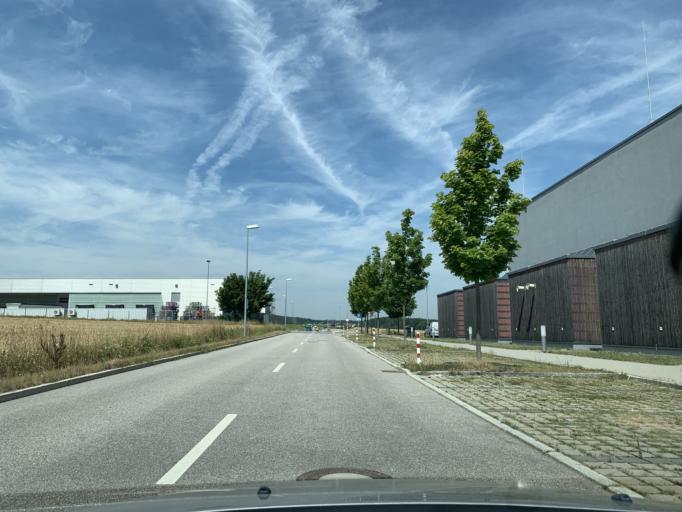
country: DE
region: Bavaria
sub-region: Lower Bavaria
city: Vilsbiburg
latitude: 48.4540
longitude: 12.3457
